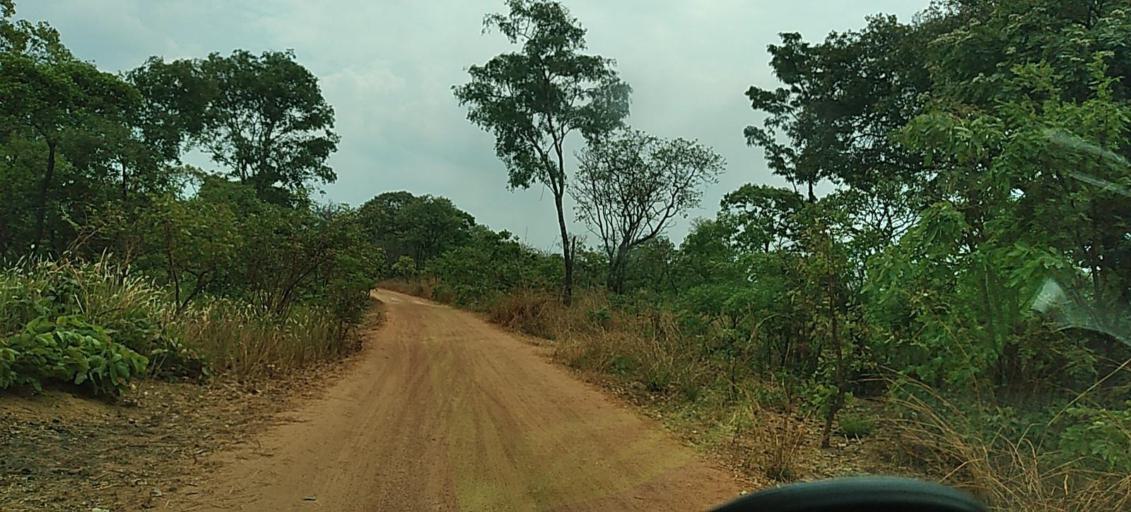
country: ZM
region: North-Western
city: Kansanshi
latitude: -12.0412
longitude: 26.3299
